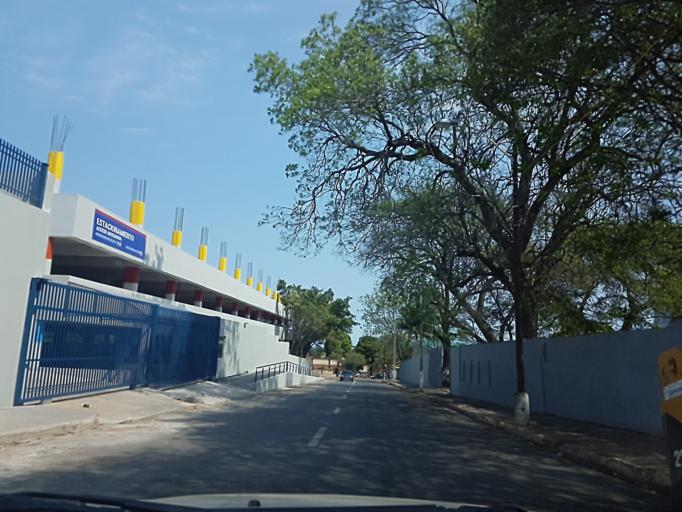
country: PY
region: Asuncion
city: Asuncion
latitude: -25.2992
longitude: -57.6387
